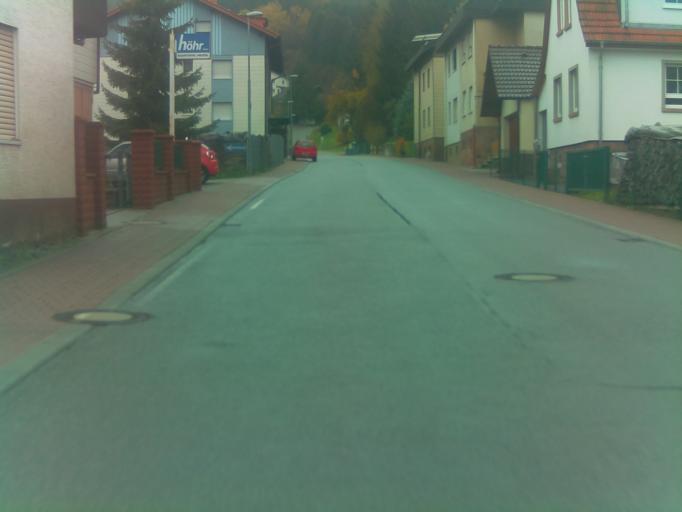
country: DE
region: Baden-Wuerttemberg
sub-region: Karlsruhe Region
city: Heiligkreuzsteinach
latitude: 49.4686
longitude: 8.7997
